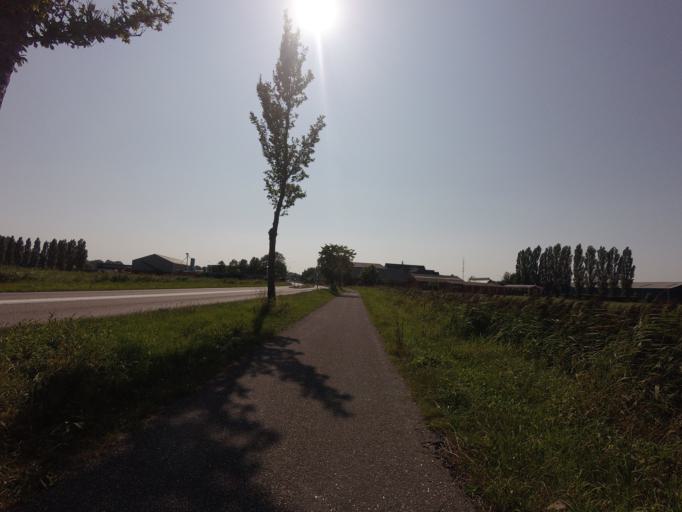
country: NL
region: Groningen
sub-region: Gemeente Zuidhorn
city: Grijpskerk
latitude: 53.2690
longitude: 6.3074
